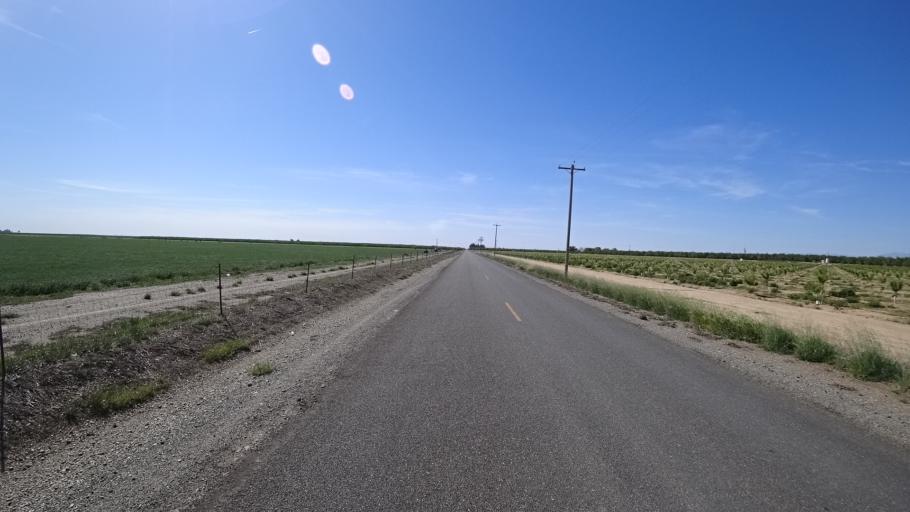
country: US
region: California
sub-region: Glenn County
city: Hamilton City
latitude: 39.6734
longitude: -122.1033
